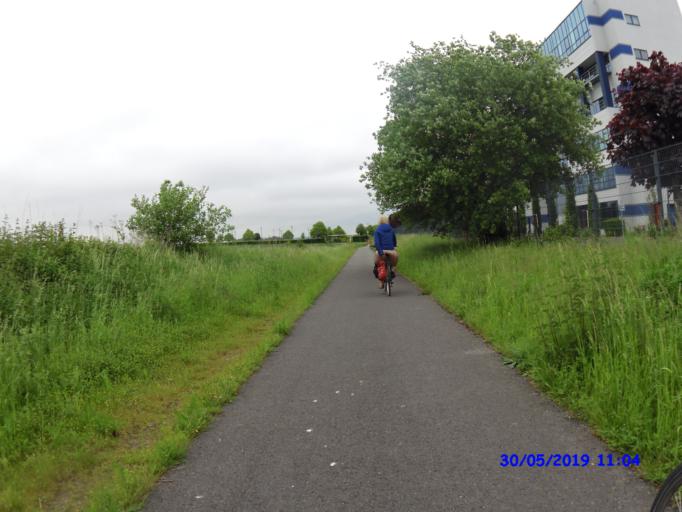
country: BE
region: Wallonia
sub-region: Province du Hainaut
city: Thuin
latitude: 50.2825
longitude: 4.3200
